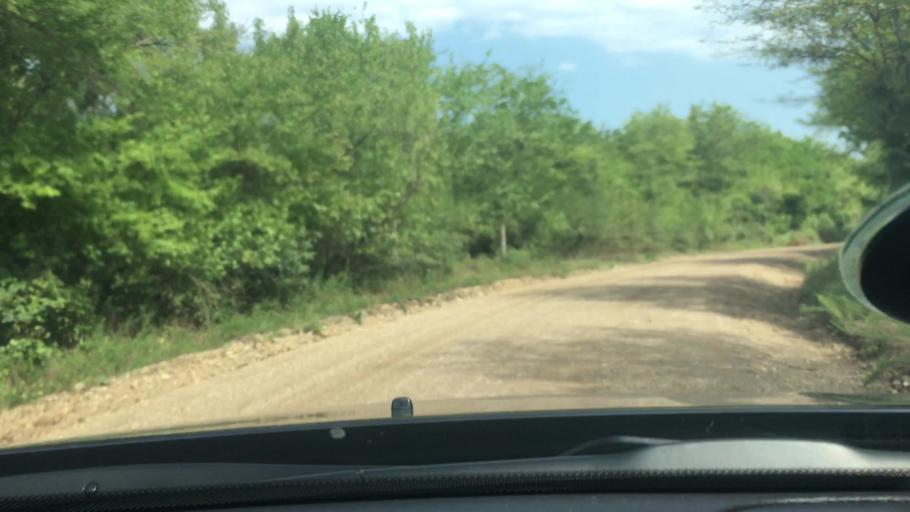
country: US
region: Oklahoma
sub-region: Atoka County
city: Atoka
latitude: 34.4423
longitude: -96.0671
